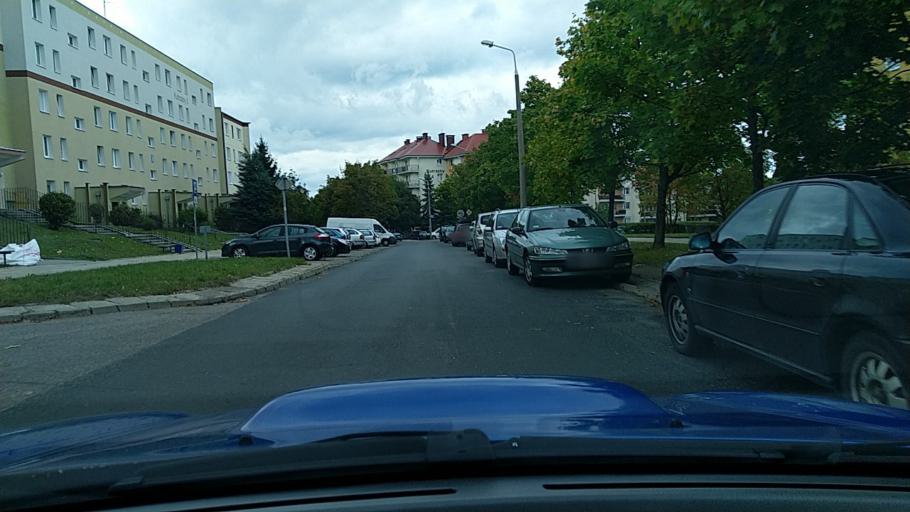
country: PL
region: Warmian-Masurian Voivodeship
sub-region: Olsztyn
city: Kortowo
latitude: 53.7405
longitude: 20.4822
